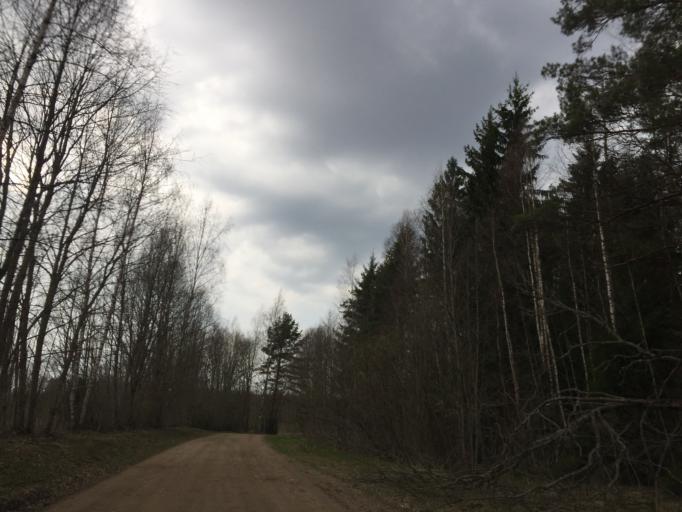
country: EE
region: Vorumaa
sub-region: Antsla vald
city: Vana-Antsla
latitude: 57.9424
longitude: 26.7213
